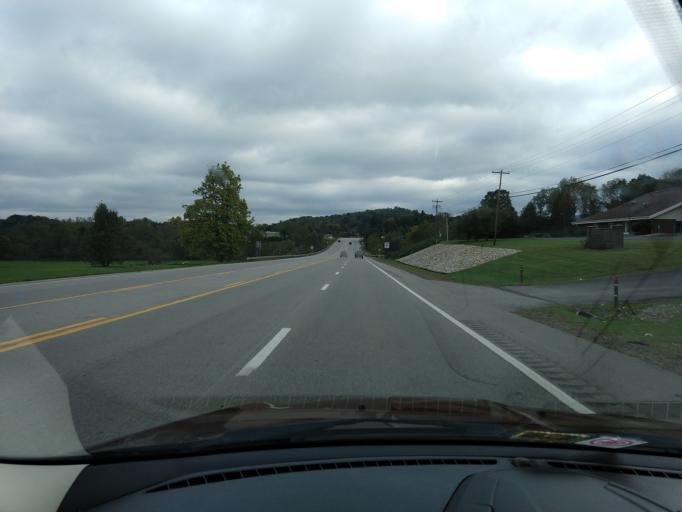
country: US
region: West Virginia
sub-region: Randolph County
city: Elkins
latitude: 38.8582
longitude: -79.8629
